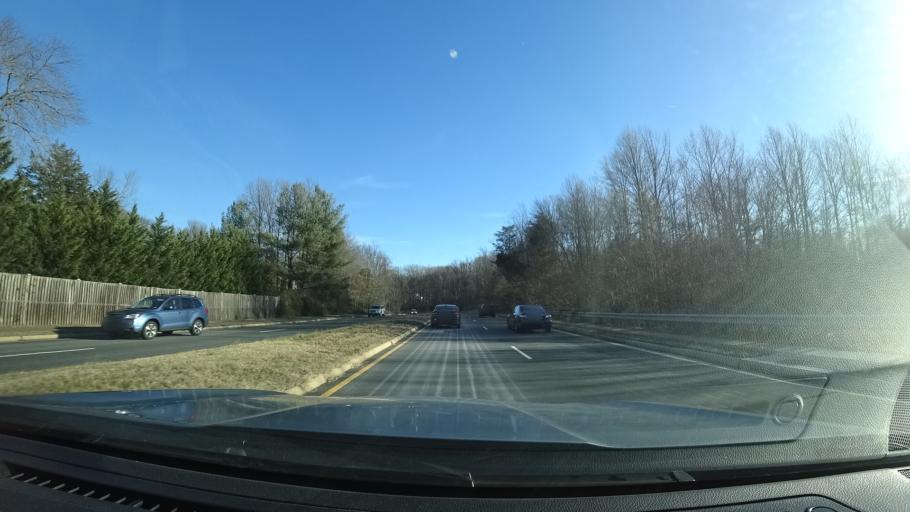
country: US
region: Virginia
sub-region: Fairfax County
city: Dranesville
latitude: 38.9893
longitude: -77.3529
